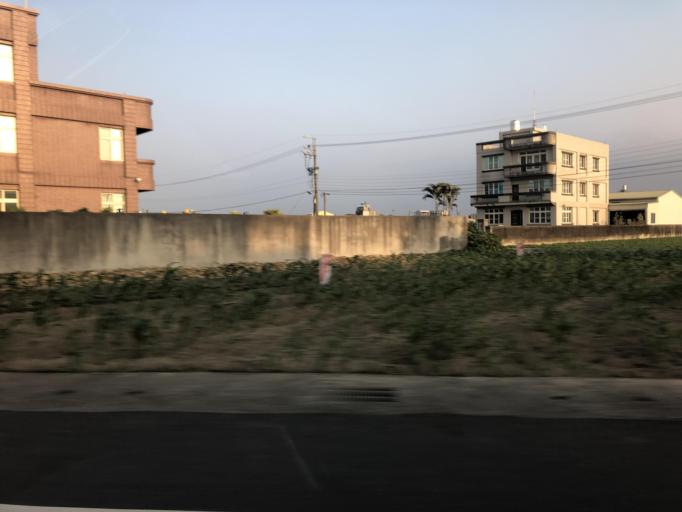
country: TW
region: Taiwan
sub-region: Tainan
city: Tainan
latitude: 23.1415
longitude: 120.2674
